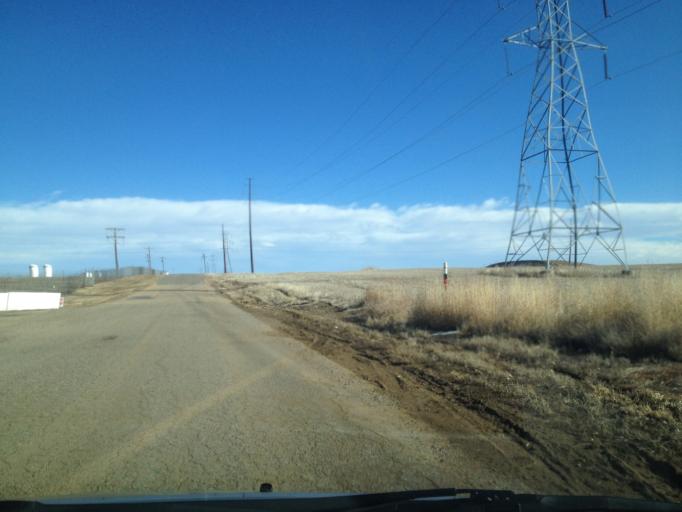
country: US
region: Colorado
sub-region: Weld County
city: Dacono
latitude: 40.0584
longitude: -104.9744
